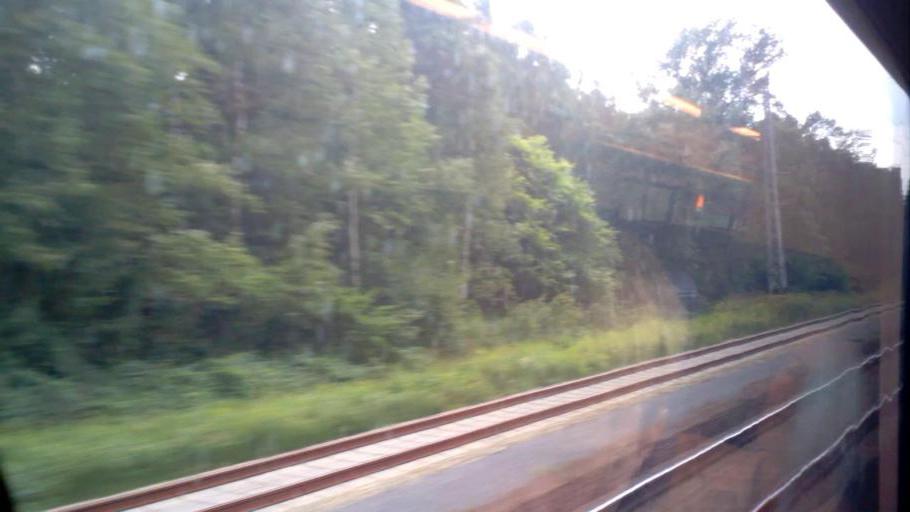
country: DE
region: Berlin
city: Lichtenrade
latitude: 52.3448
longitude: 13.3758
